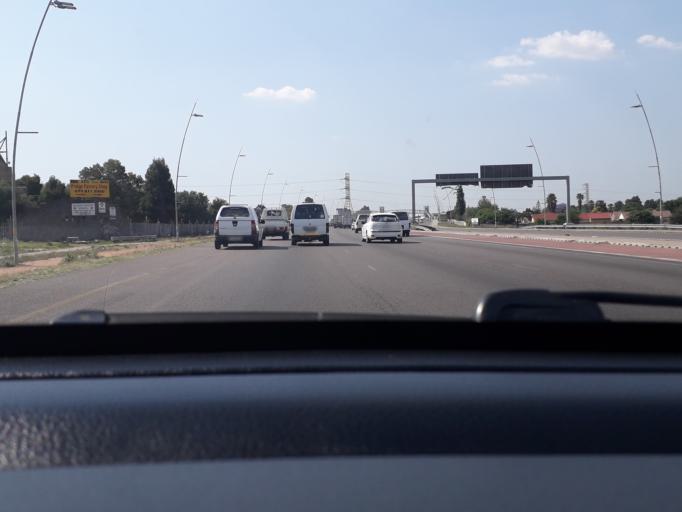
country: ZA
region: Gauteng
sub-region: City of Johannesburg Metropolitan Municipality
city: Modderfontein
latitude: -26.0847
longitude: 28.1899
